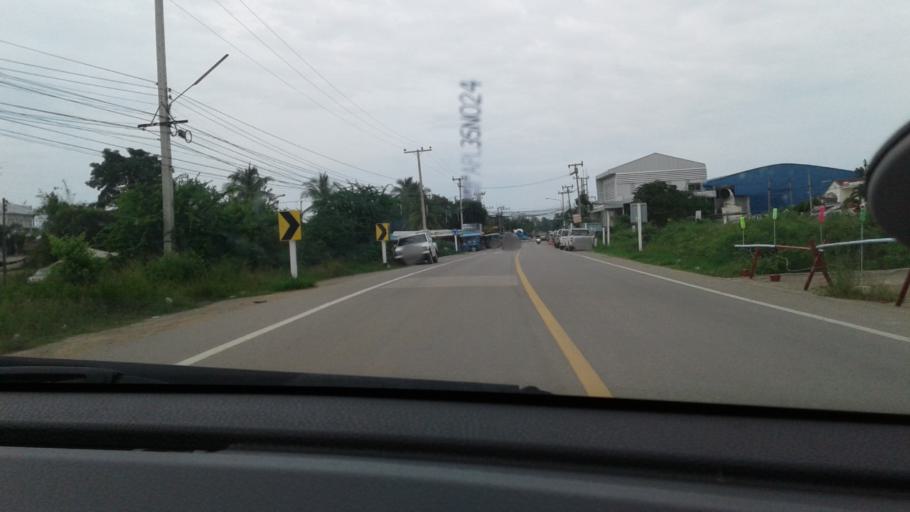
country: TH
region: Prachuap Khiri Khan
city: Pran Buri
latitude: 12.3883
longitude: 99.9850
